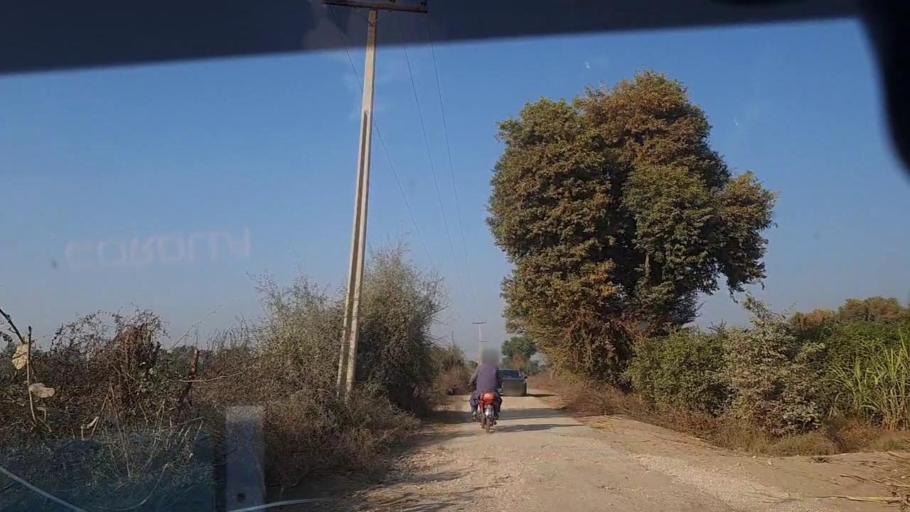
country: PK
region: Sindh
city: Sobhadero
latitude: 27.2507
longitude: 68.3501
